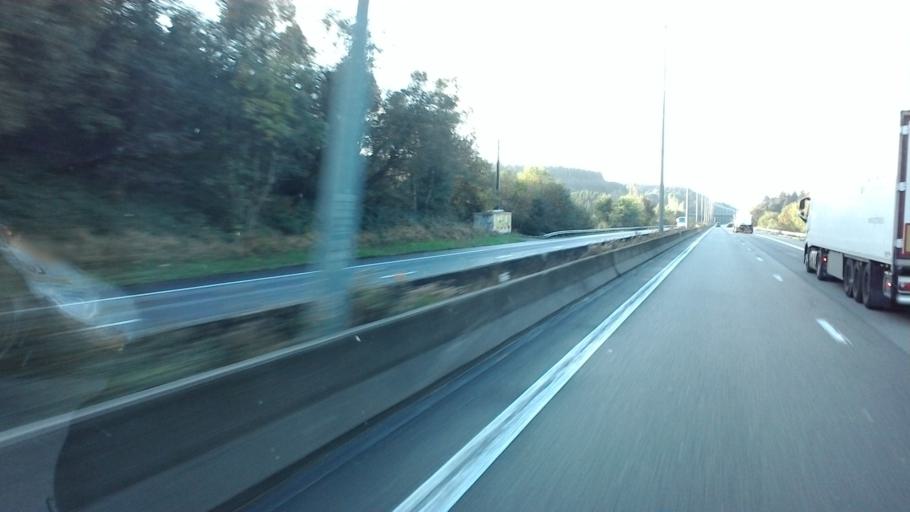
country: BE
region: Wallonia
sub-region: Province du Luxembourg
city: Manhay
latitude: 50.3387
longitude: 5.6940
